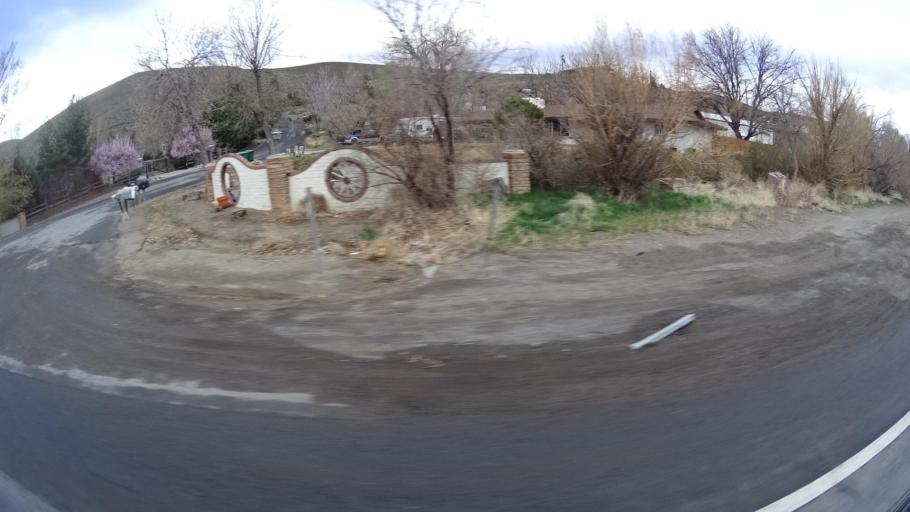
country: US
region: Nevada
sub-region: Storey County
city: Virginia City
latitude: 39.3714
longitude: -119.7473
